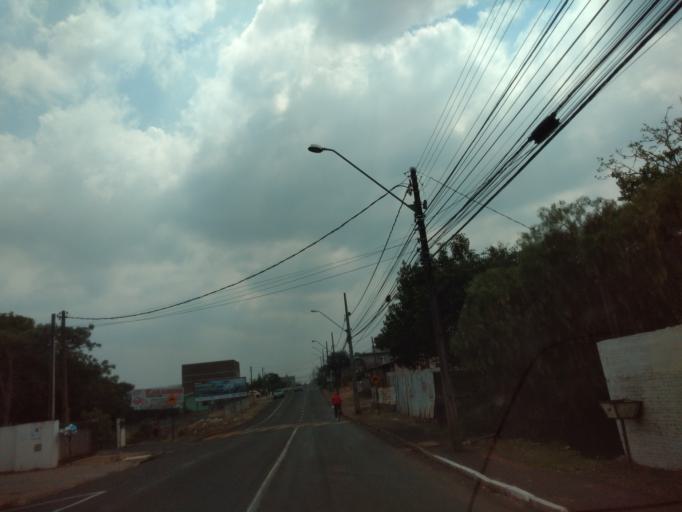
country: BR
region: Parana
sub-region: Guarapuava
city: Guarapuava
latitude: -25.3825
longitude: -51.4810
